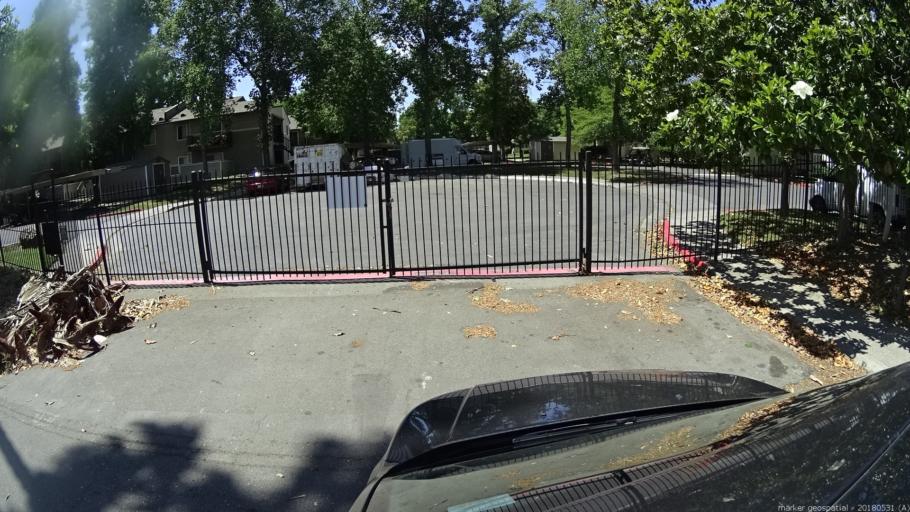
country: US
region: California
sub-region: Sacramento County
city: Sacramento
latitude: 38.6163
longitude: -121.5087
